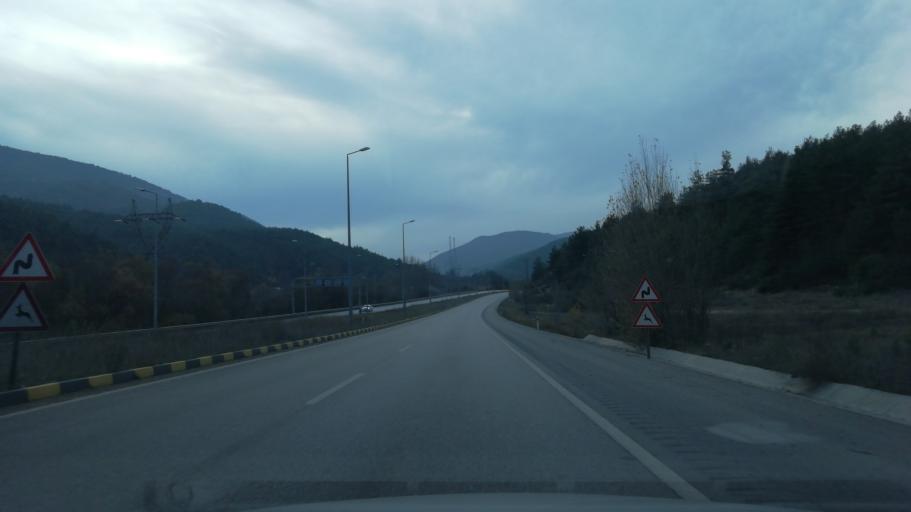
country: TR
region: Karabuk
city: Karabuk
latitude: 41.0787
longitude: 32.6683
